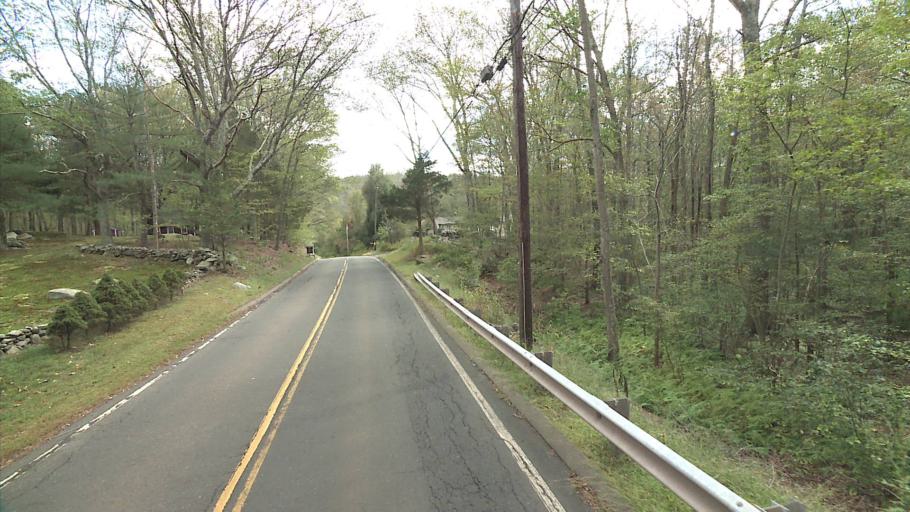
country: US
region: Connecticut
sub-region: Middlesex County
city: Durham
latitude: 41.4223
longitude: -72.6297
